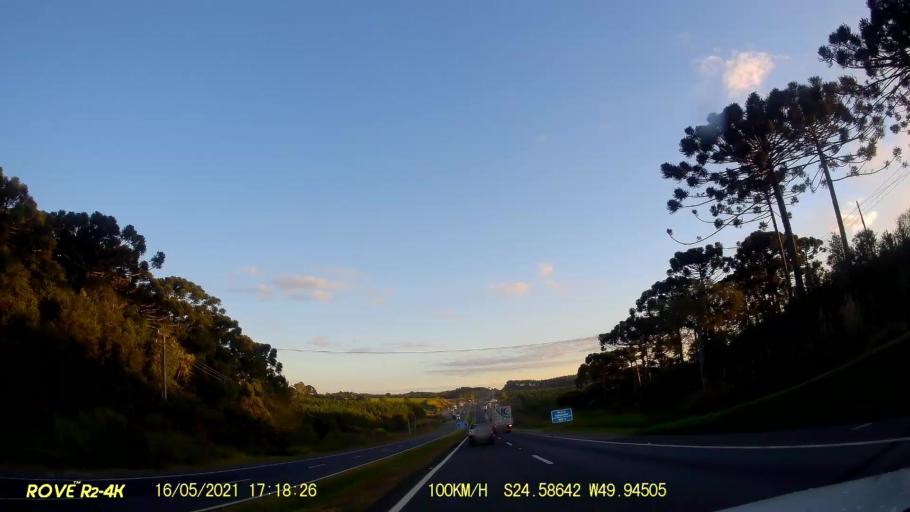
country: BR
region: Parana
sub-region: Pirai Do Sul
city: Pirai do Sul
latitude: -24.5868
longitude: -49.9452
